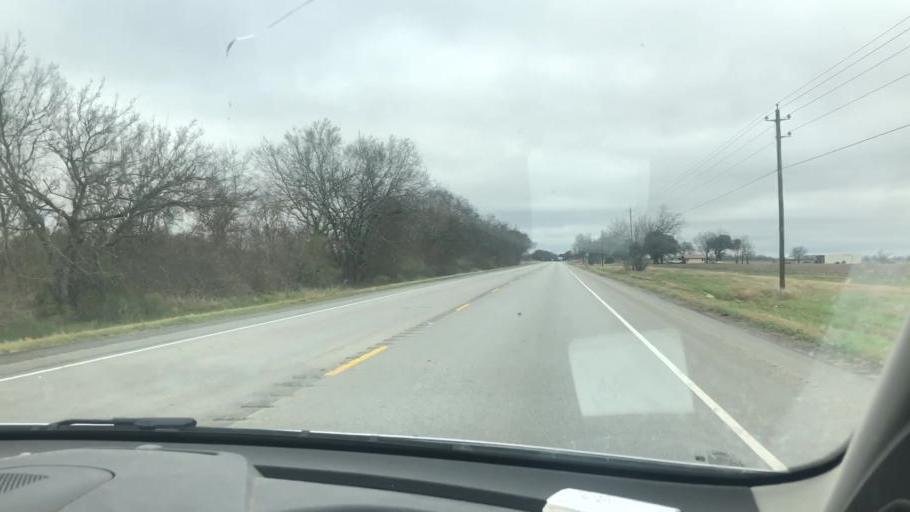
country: US
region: Texas
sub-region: Matagorda County
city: Bay City
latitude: 29.0716
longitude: -95.9718
